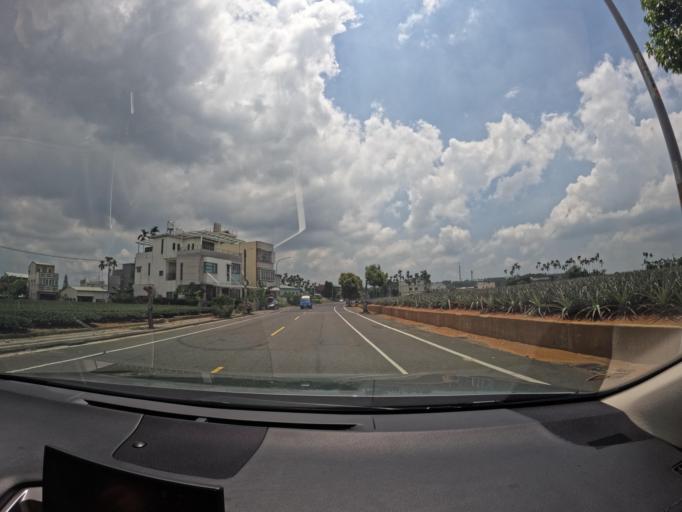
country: TW
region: Taiwan
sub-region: Nantou
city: Nantou
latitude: 23.9044
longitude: 120.6375
